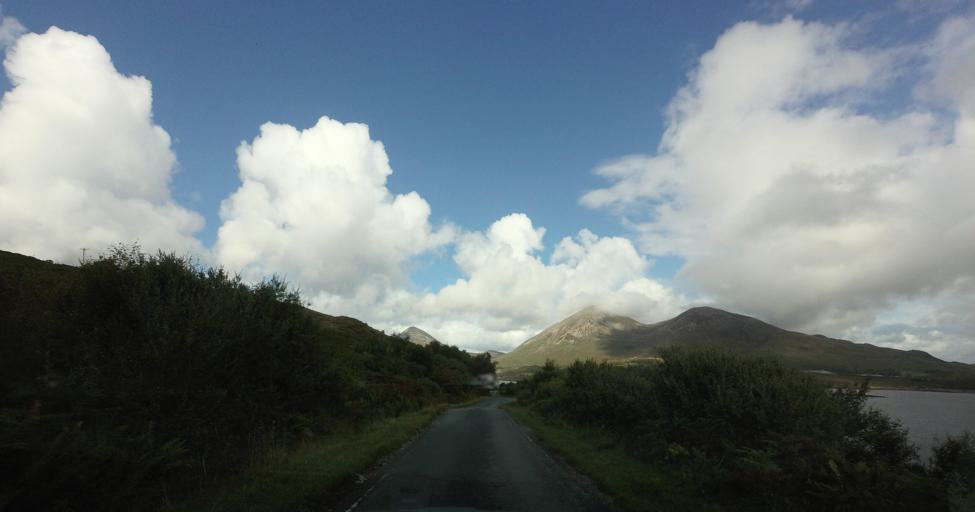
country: GB
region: Scotland
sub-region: Highland
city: Portree
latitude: 57.1963
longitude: -6.0285
